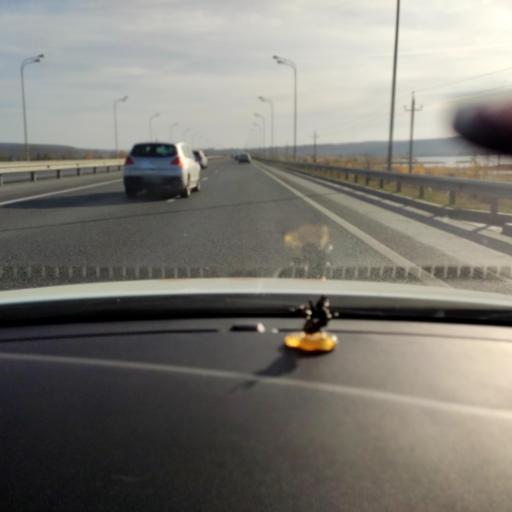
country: RU
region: Tatarstan
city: Osinovo
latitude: 55.8098
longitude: 48.8417
